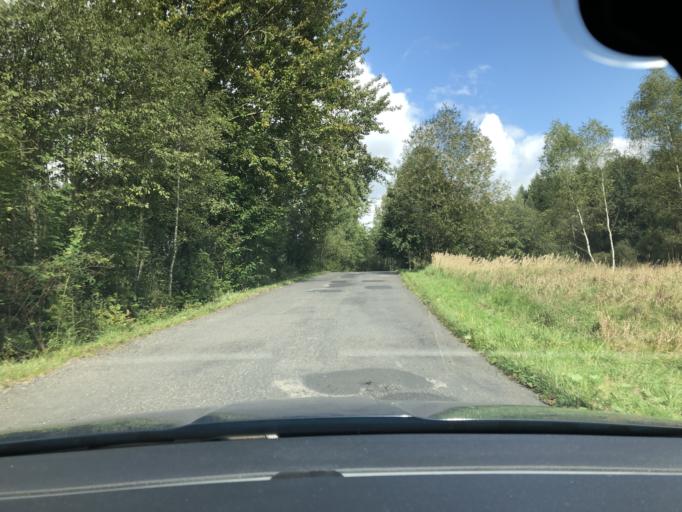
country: PL
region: Silesian Voivodeship
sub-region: Powiat zywiecki
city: Slemien
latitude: 49.7121
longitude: 19.4205
